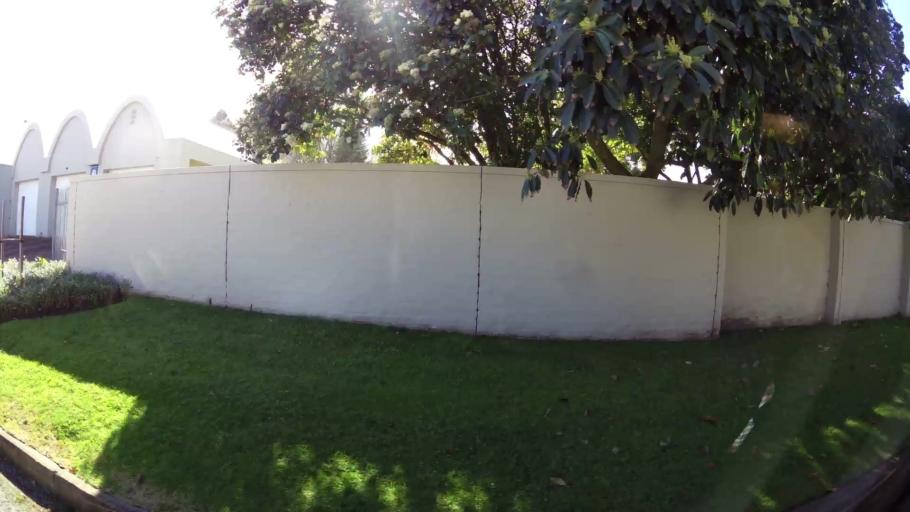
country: ZA
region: Western Cape
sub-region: Eden District Municipality
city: George
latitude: -33.9482
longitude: 22.4583
